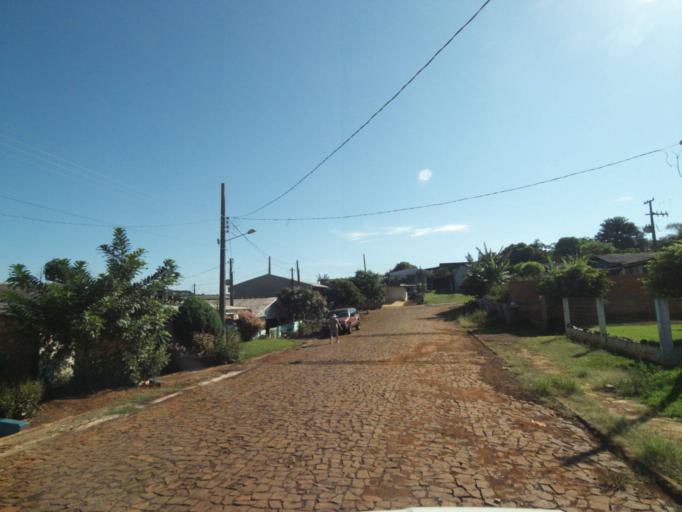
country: BR
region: Parana
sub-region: Laranjeiras Do Sul
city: Laranjeiras do Sul
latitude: -25.4936
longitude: -52.5359
